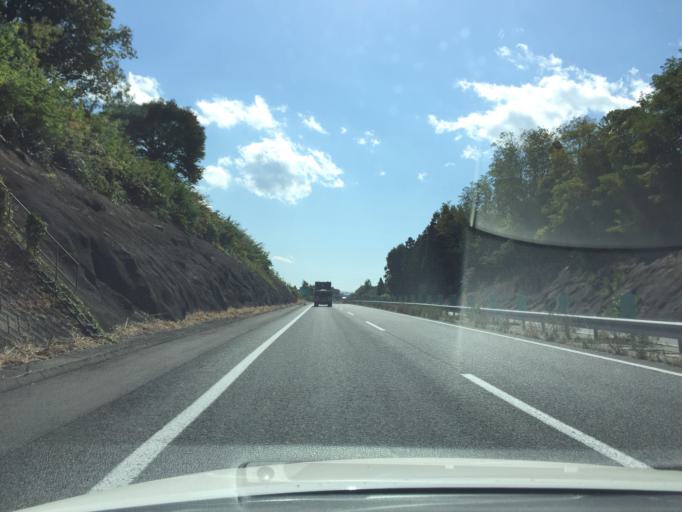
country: JP
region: Fukushima
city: Sukagawa
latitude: 37.2788
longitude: 140.3506
